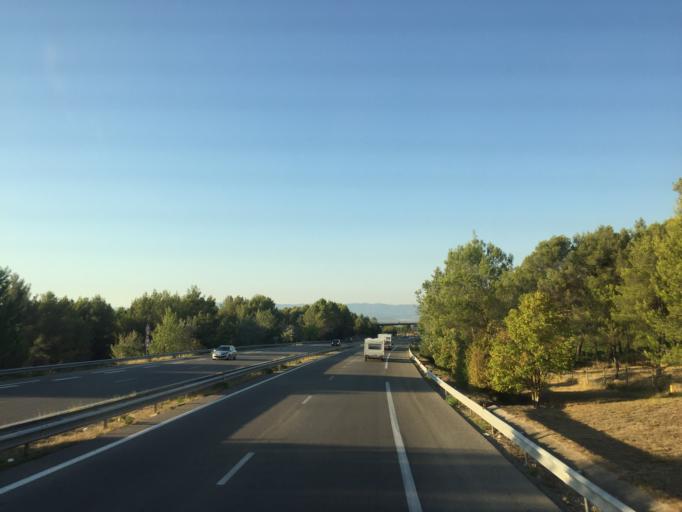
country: FR
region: Provence-Alpes-Cote d'Azur
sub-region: Departement des Bouches-du-Rhone
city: Venelles
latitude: 43.6262
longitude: 5.4925
